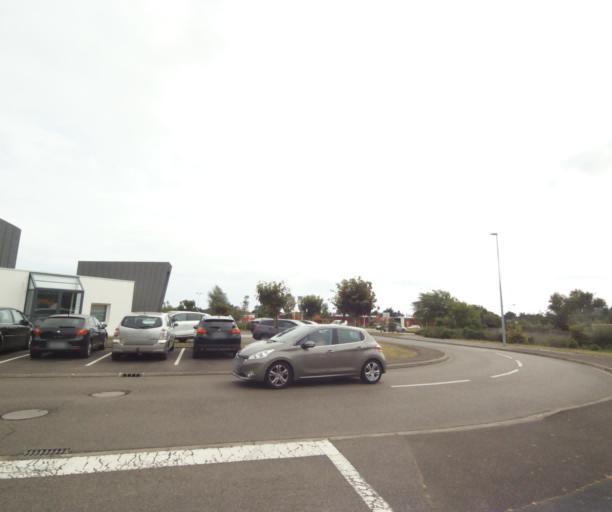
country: FR
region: Pays de la Loire
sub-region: Departement de la Vendee
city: Chateau-d'Olonne
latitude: 46.4886
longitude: -1.7456
